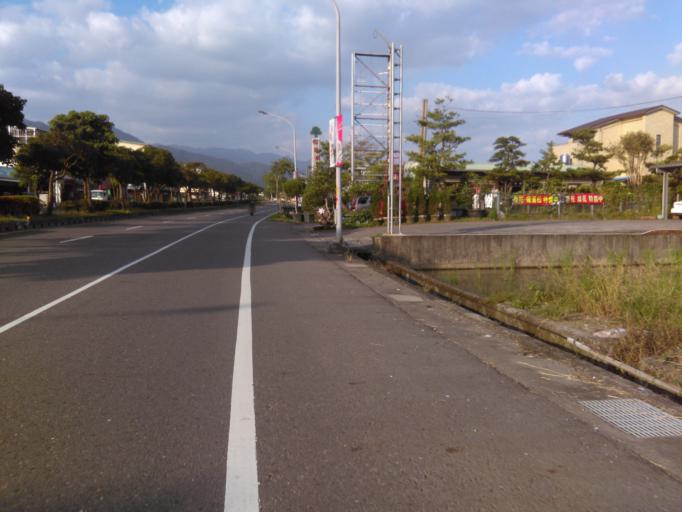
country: TW
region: Taiwan
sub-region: Yilan
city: Yilan
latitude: 24.8056
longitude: 121.7659
